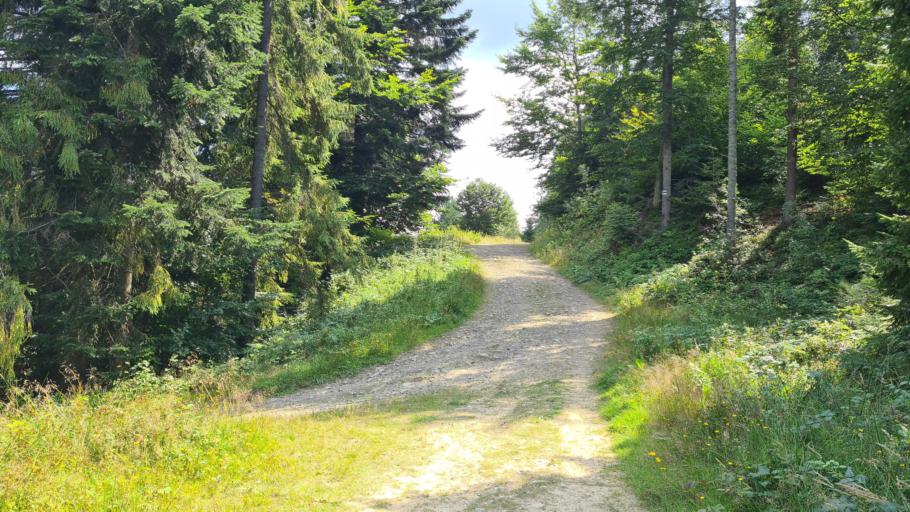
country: PL
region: Lesser Poland Voivodeship
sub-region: Powiat nowosadecki
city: Rytro
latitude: 49.4100
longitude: 20.6284
